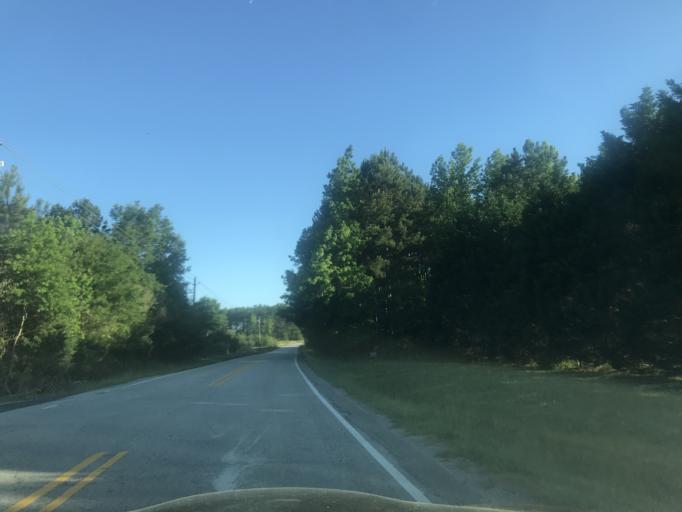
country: US
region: North Carolina
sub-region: Johnston County
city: Archer Lodge
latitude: 35.7096
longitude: -78.3850
